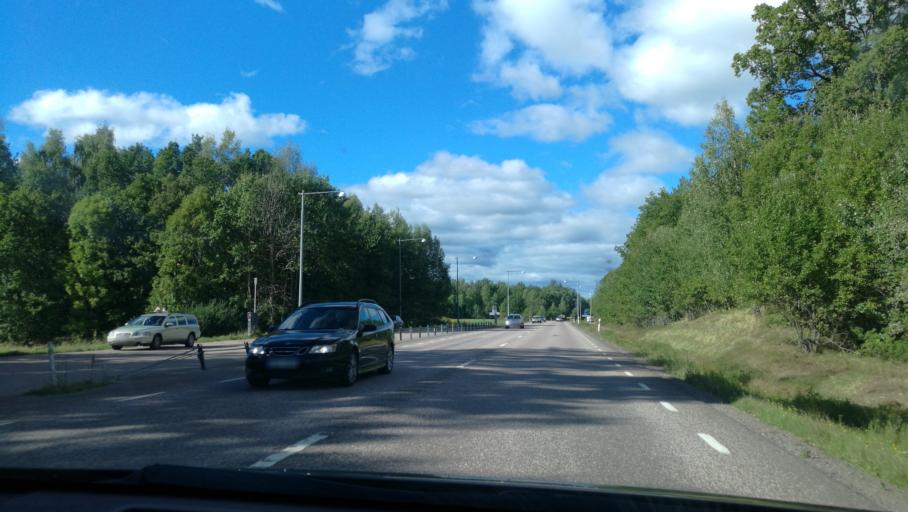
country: SE
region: Soedermanland
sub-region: Eskilstuna Kommun
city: Kvicksund
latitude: 59.4711
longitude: 16.3095
